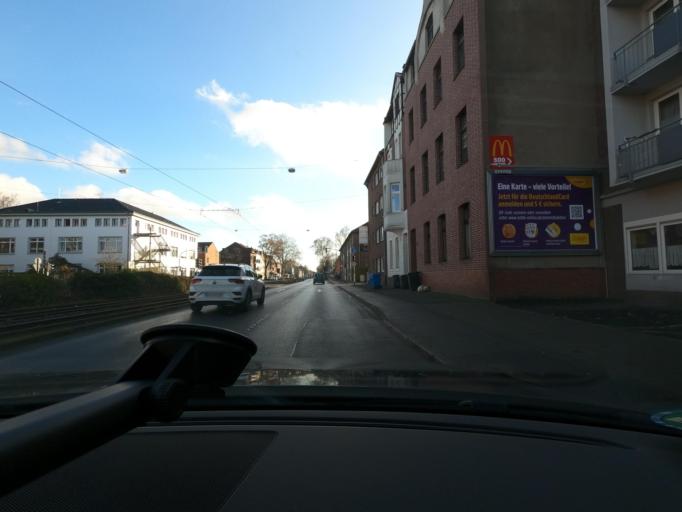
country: DE
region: North Rhine-Westphalia
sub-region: Regierungsbezirk Dusseldorf
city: Krefeld
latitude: 51.3521
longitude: 6.5368
